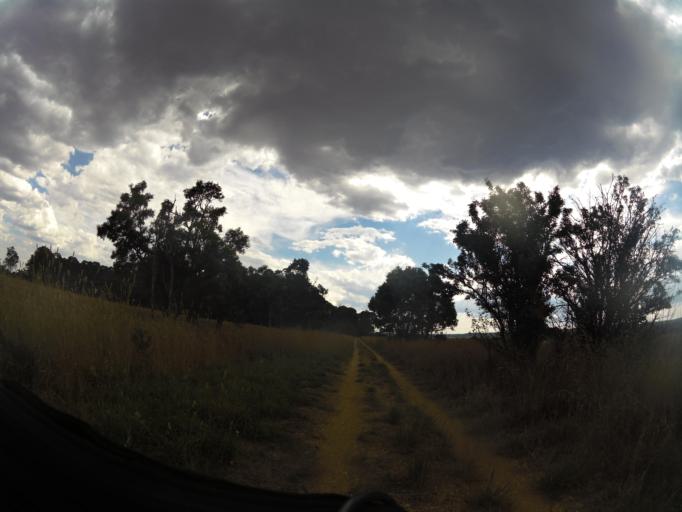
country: AU
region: Victoria
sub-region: Wellington
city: Heyfield
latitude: -38.0165
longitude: 146.6884
